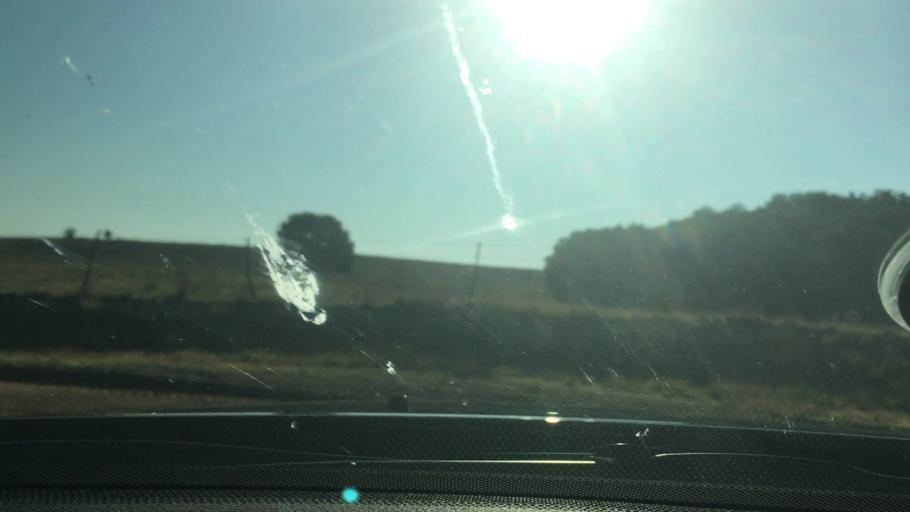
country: US
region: Oklahoma
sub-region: Murray County
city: Sulphur
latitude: 34.4049
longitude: -96.7938
